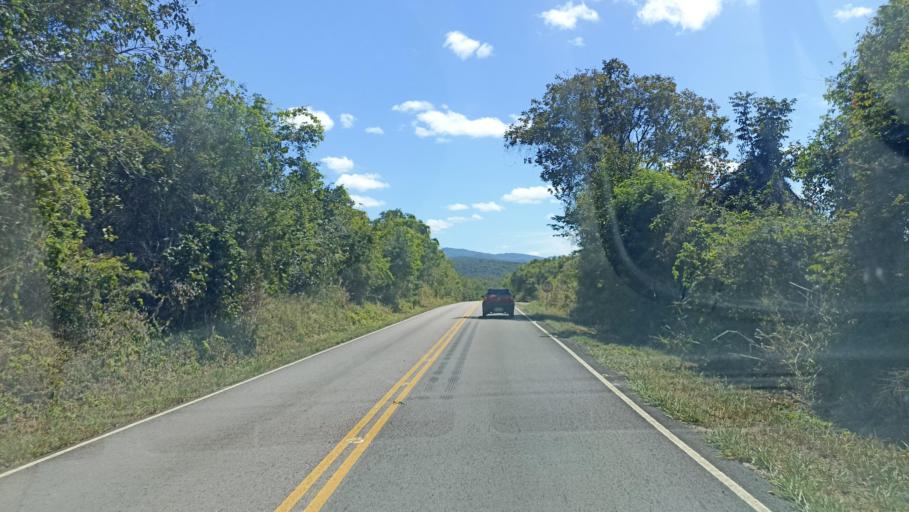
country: BR
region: Bahia
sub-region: Andarai
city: Vera Cruz
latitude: -12.7606
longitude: -41.3270
